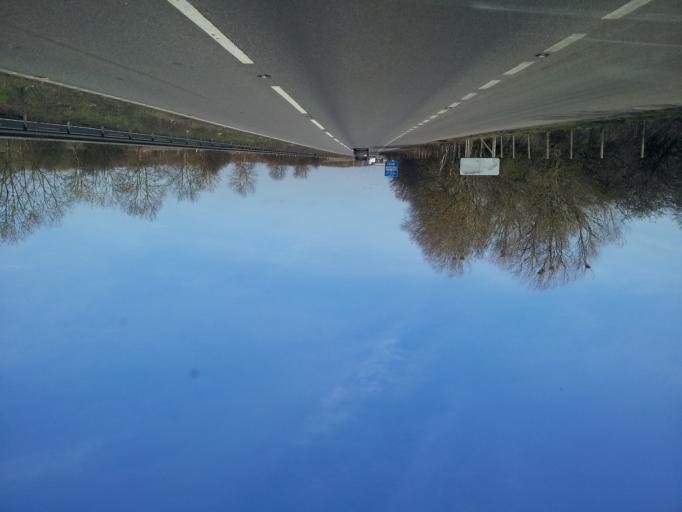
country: GB
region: England
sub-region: Cambridgeshire
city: Great Stukeley
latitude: 52.3541
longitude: -0.2525
